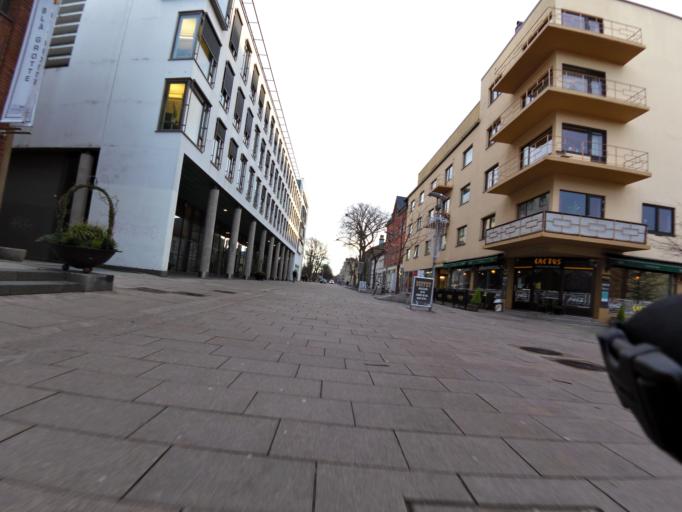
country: NO
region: Ostfold
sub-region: Fredrikstad
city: Fredrikstad
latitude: 59.2107
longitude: 10.9394
